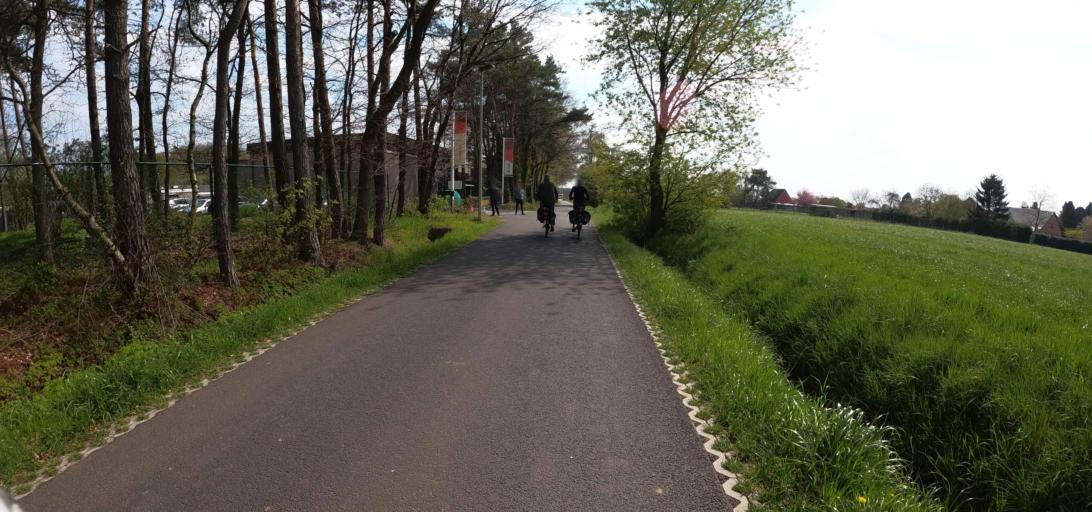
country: BE
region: Flanders
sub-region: Provincie Antwerpen
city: Oostmalle
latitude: 51.3062
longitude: 4.7476
